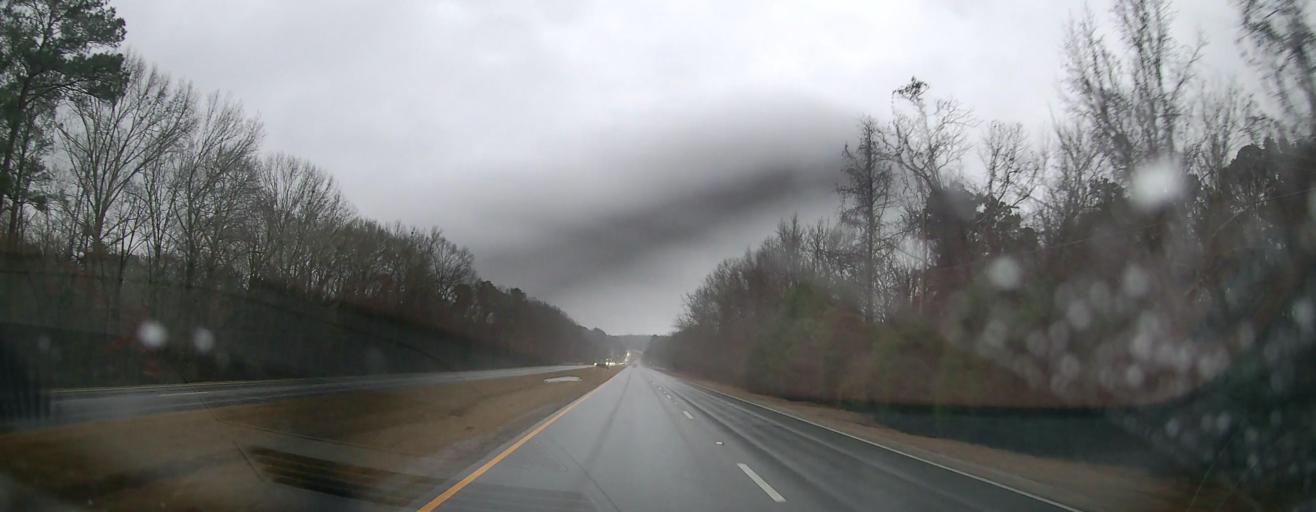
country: US
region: Alabama
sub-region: Morgan County
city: Flint City
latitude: 34.4982
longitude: -86.9667
